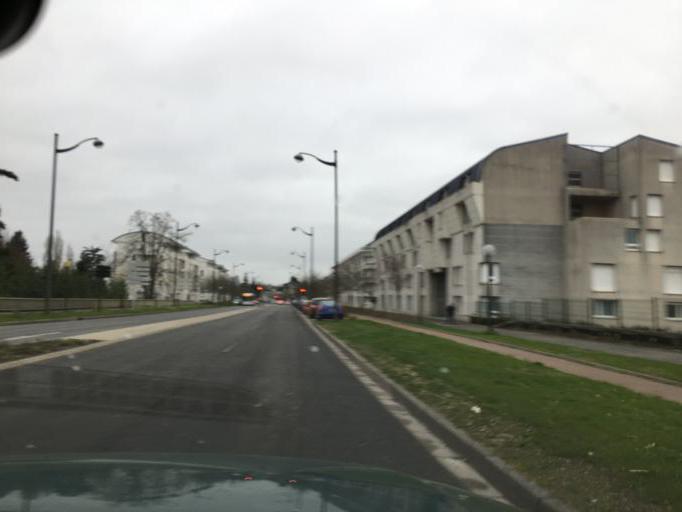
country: FR
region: Centre
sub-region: Departement du Loiret
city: Saint-Jean-le-Blanc
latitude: 47.9044
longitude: 1.9188
